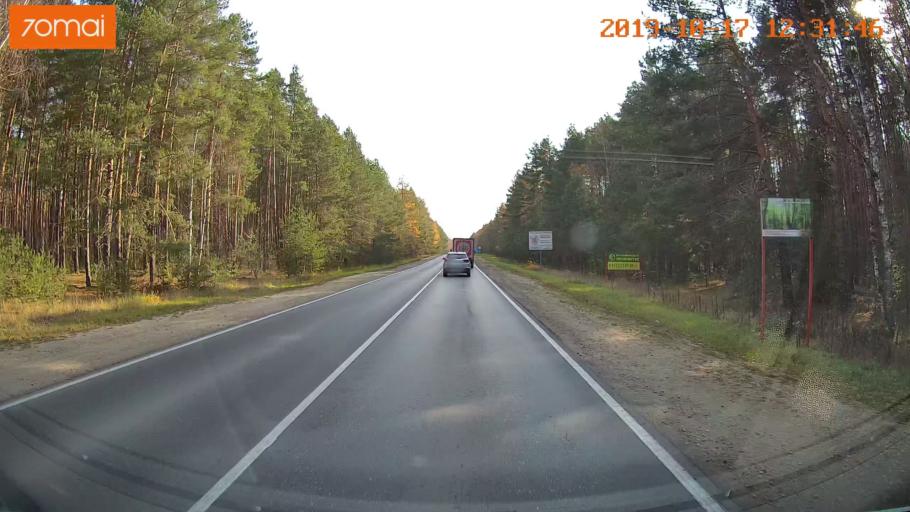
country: RU
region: Rjazan
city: Syntul
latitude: 54.9657
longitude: 41.3376
